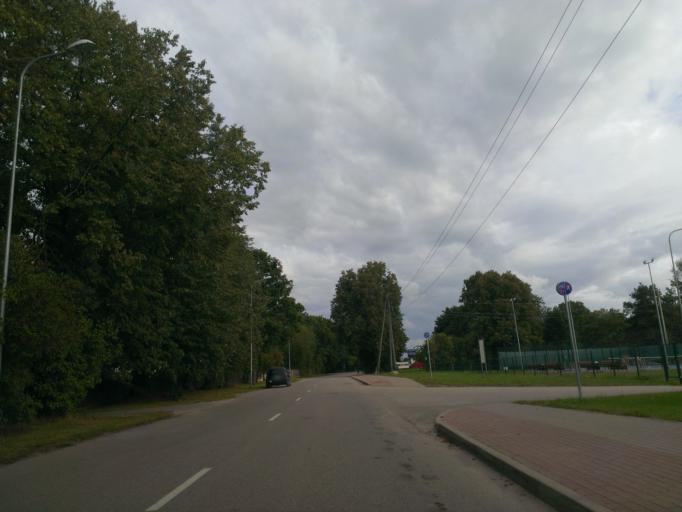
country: LV
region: Ikskile
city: Ikskile
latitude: 56.8311
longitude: 24.4859
